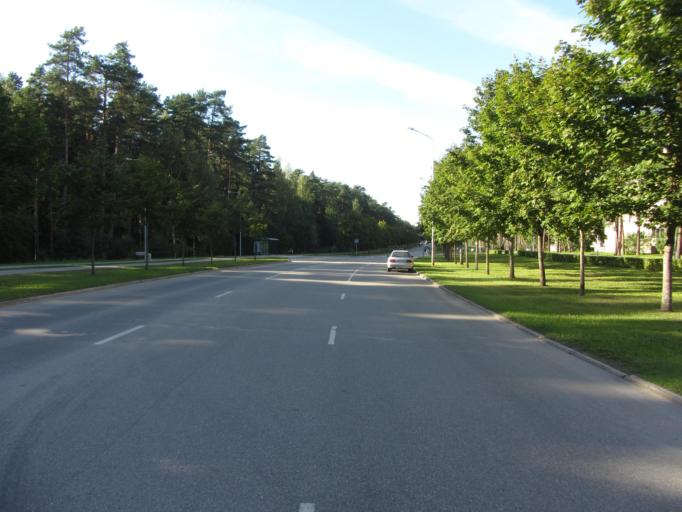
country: LT
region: Utenos apskritis
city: Visaginas
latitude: 55.5883
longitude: 26.4426
